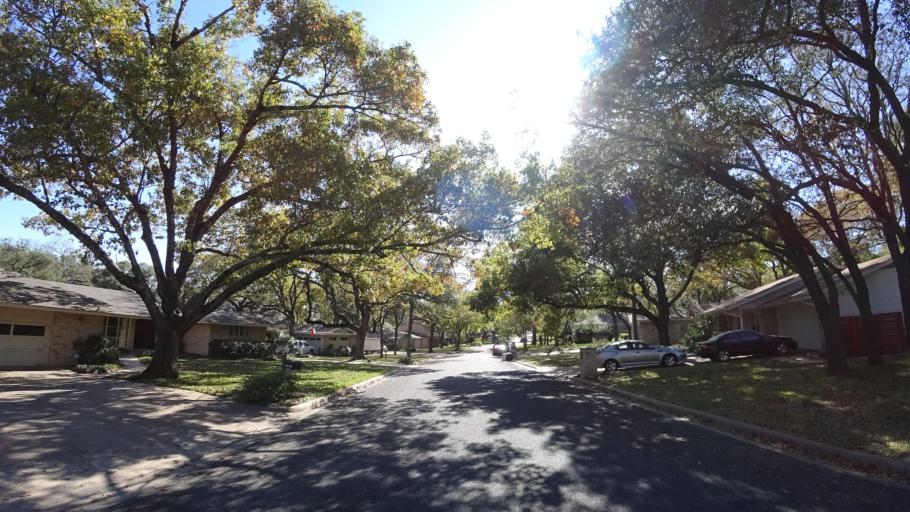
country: US
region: Texas
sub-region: Williamson County
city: Jollyville
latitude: 30.3775
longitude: -97.7429
